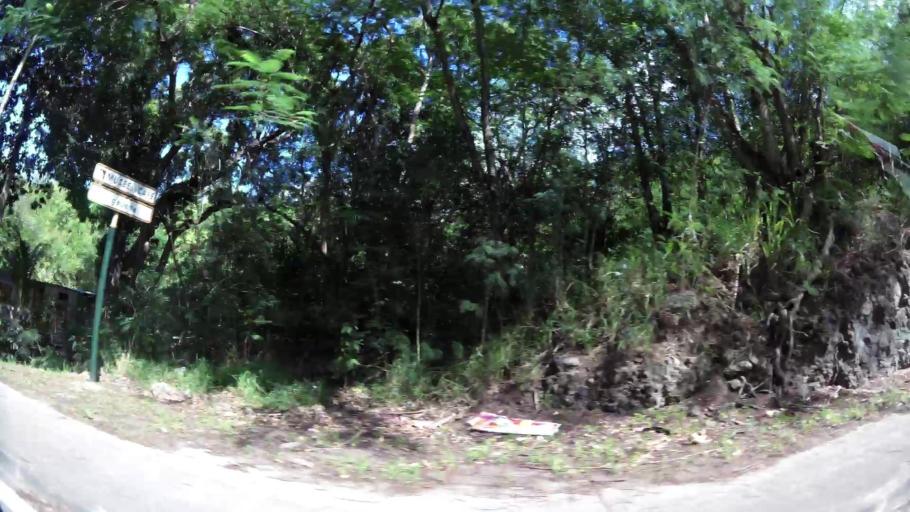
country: GP
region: Guadeloupe
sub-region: Guadeloupe
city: Vieux-Habitants
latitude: 16.0614
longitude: -61.7589
